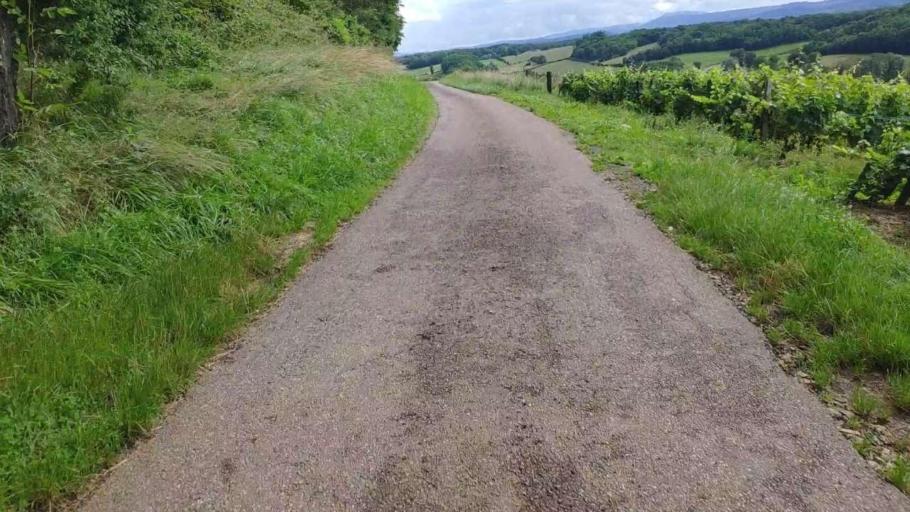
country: FR
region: Franche-Comte
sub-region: Departement du Jura
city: Poligny
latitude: 46.8296
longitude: 5.5915
